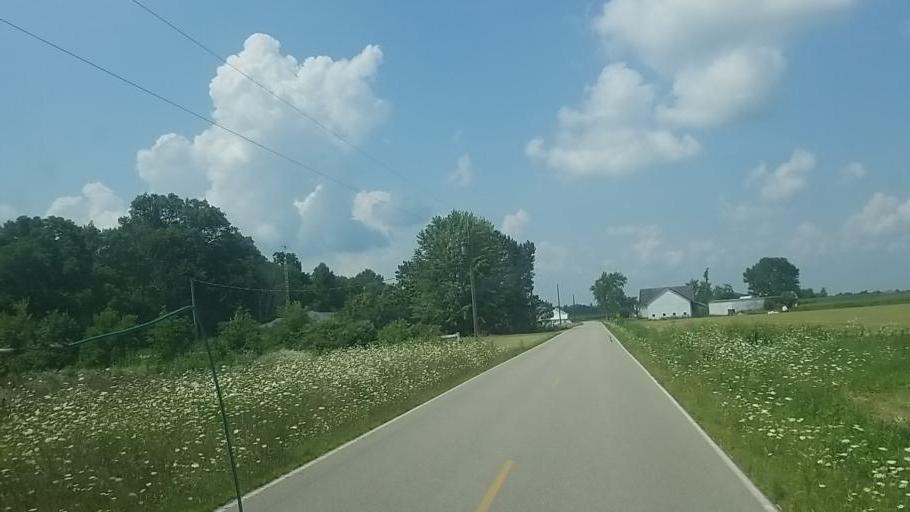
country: US
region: Ohio
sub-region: Crawford County
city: Crestline
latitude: 40.8072
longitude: -82.7545
